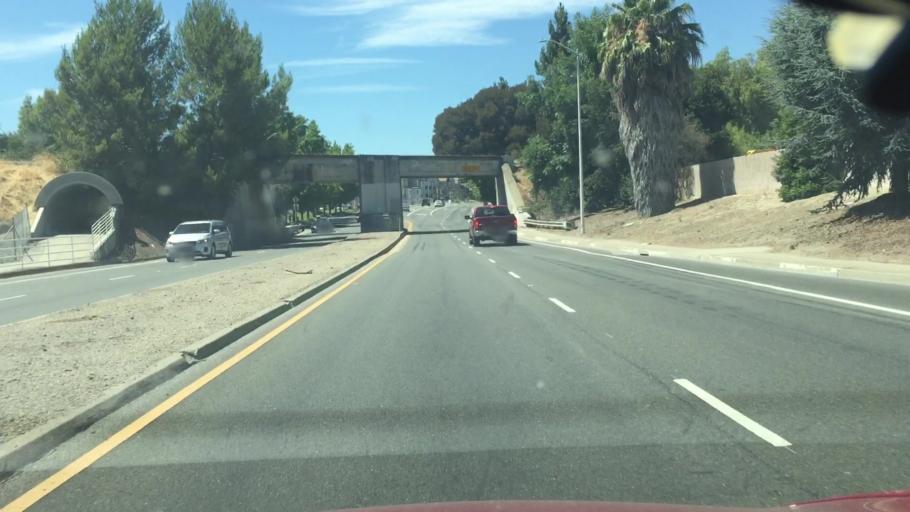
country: US
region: California
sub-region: Alameda County
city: Fremont
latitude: 37.5594
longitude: -121.9551
